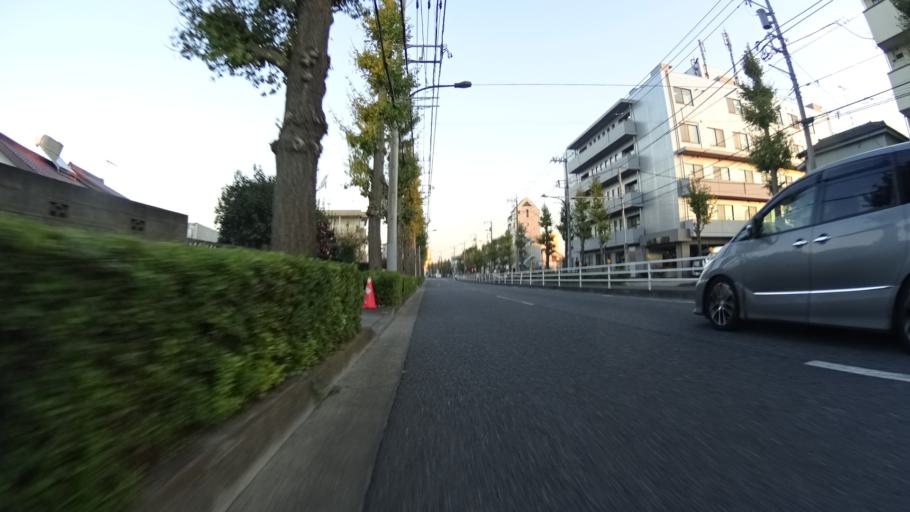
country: JP
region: Tokyo
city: Fussa
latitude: 35.7030
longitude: 139.3560
